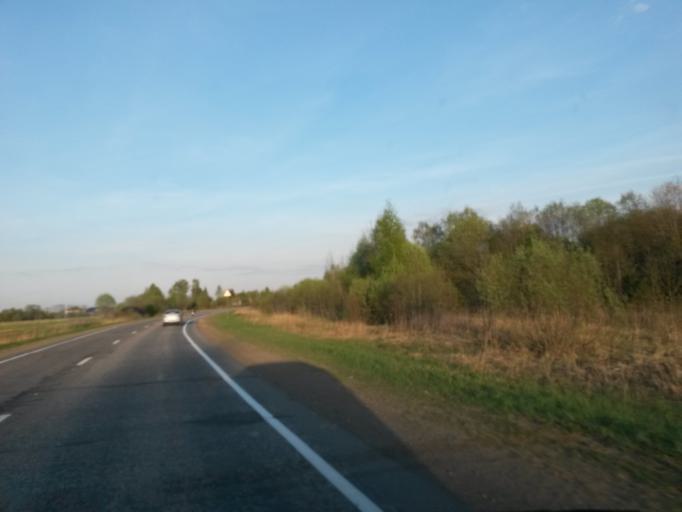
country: RU
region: Jaroslavl
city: Konstantinovskiy
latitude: 57.6711
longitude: 39.6767
